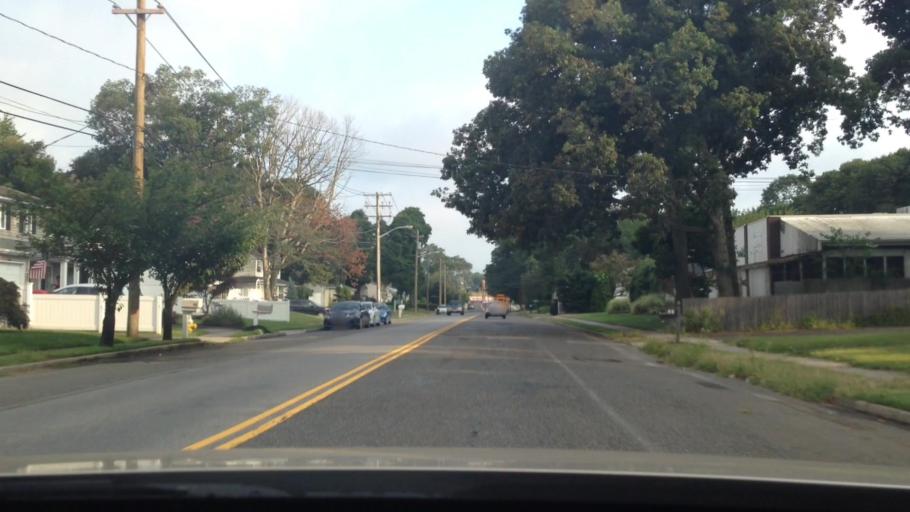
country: US
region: New York
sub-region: Suffolk County
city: Selden
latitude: 40.8600
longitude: -73.0471
